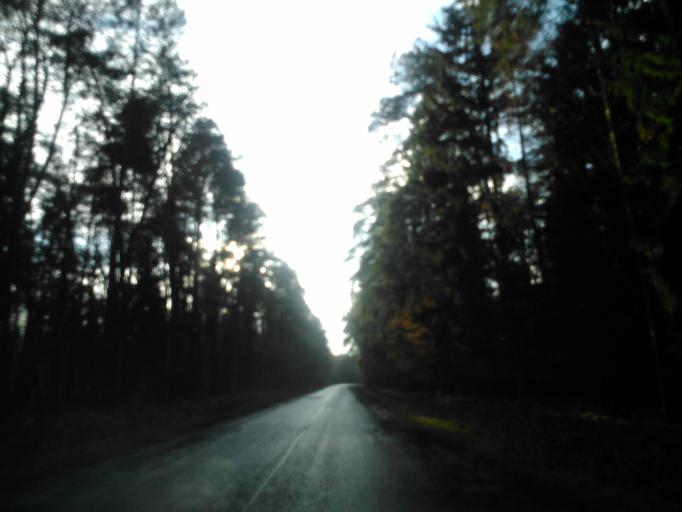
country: PL
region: Kujawsko-Pomorskie
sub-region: Powiat golubsko-dobrzynski
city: Golub-Dobrzyn
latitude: 53.1640
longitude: 19.1301
